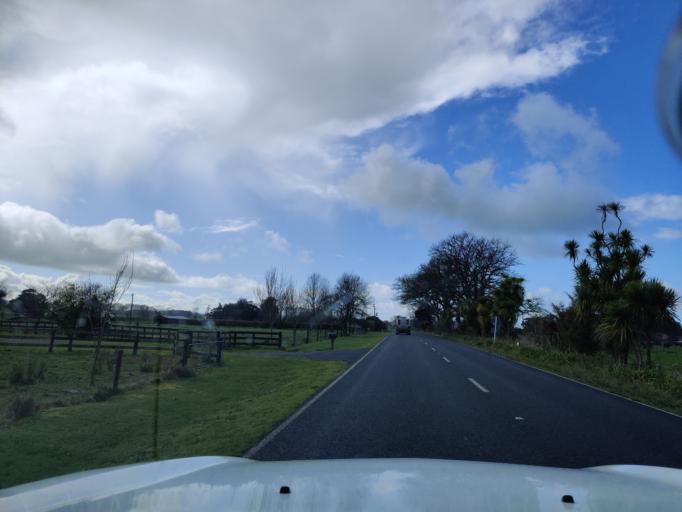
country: NZ
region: Waikato
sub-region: Waikato District
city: Ngaruawahia
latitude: -37.5679
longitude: 175.2588
